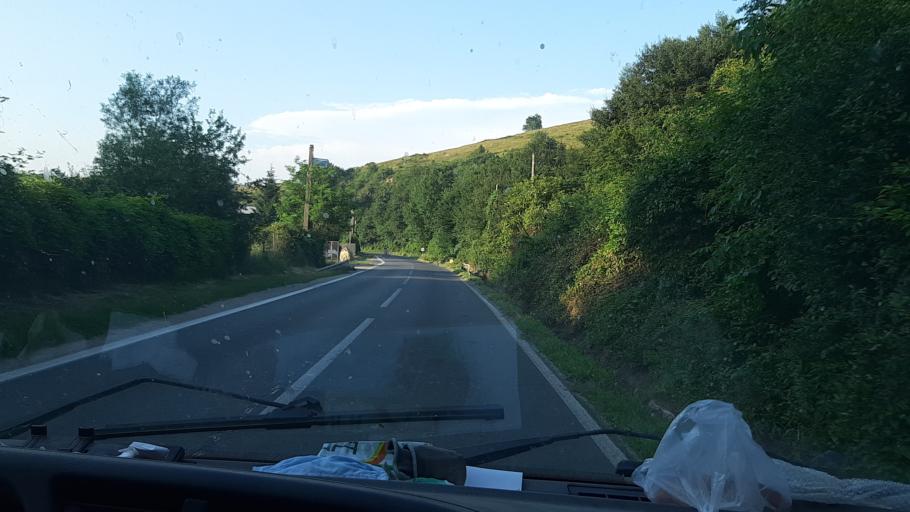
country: RO
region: Caras-Severin
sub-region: Municipiul Resita
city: Calnic
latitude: 45.3474
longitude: 21.8352
